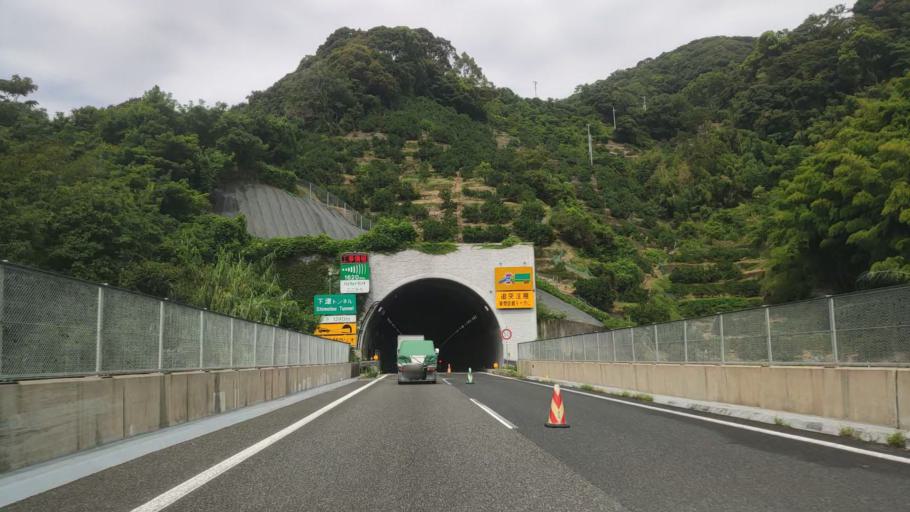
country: JP
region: Wakayama
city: Kainan
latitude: 34.1147
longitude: 135.2000
